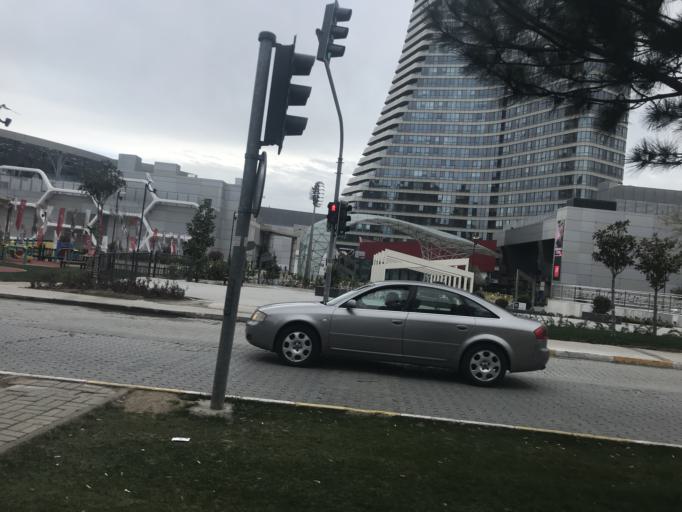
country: TR
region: Istanbul
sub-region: Atasehir
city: Atasehir
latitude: 40.9930
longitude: 29.1243
